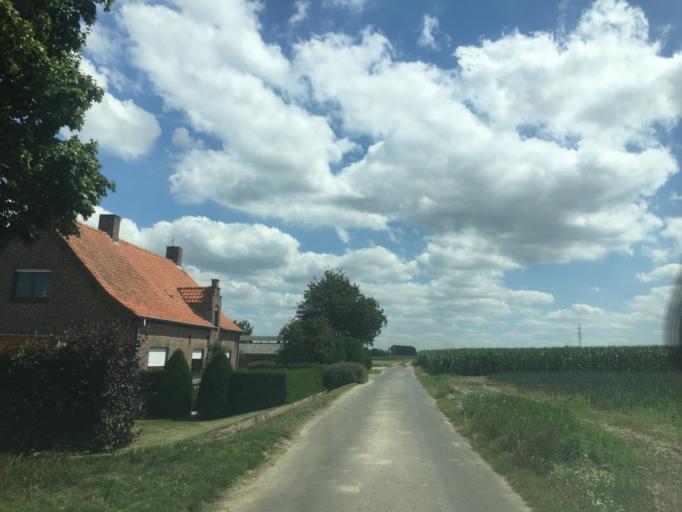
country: BE
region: Flanders
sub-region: Provincie West-Vlaanderen
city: Staden
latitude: 50.9624
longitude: 3.0063
